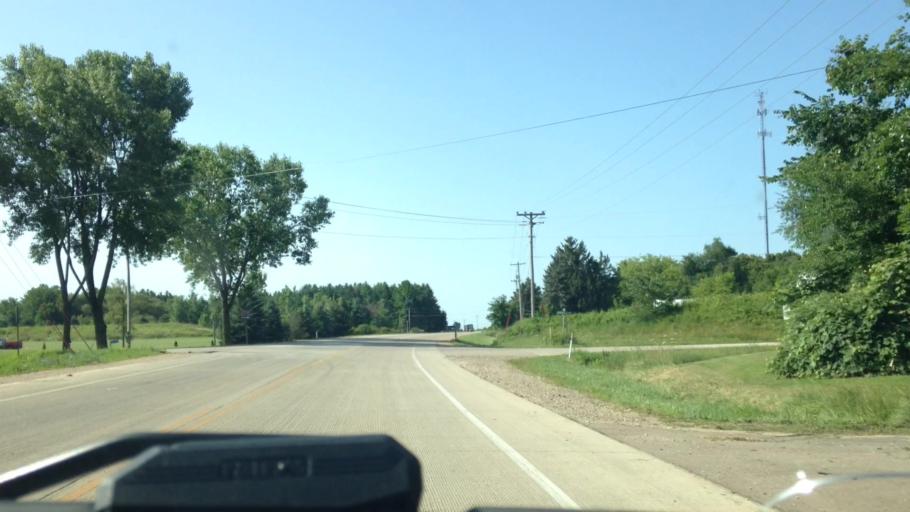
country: US
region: Wisconsin
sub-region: Dodge County
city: Mayville
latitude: 43.4583
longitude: -88.5615
